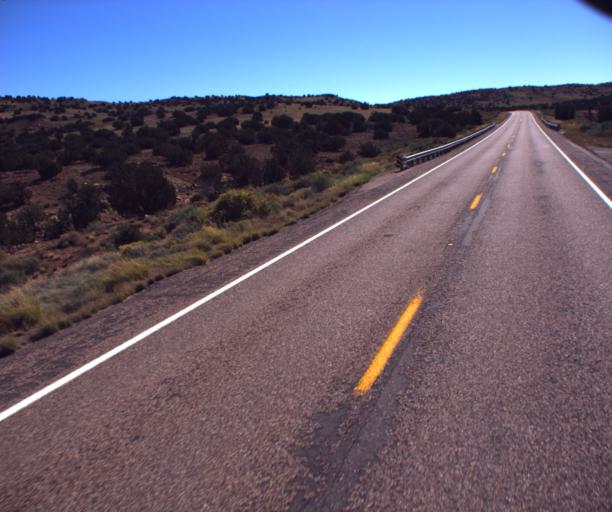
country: US
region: Arizona
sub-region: Apache County
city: Saint Johns
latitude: 34.5770
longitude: -109.5318
